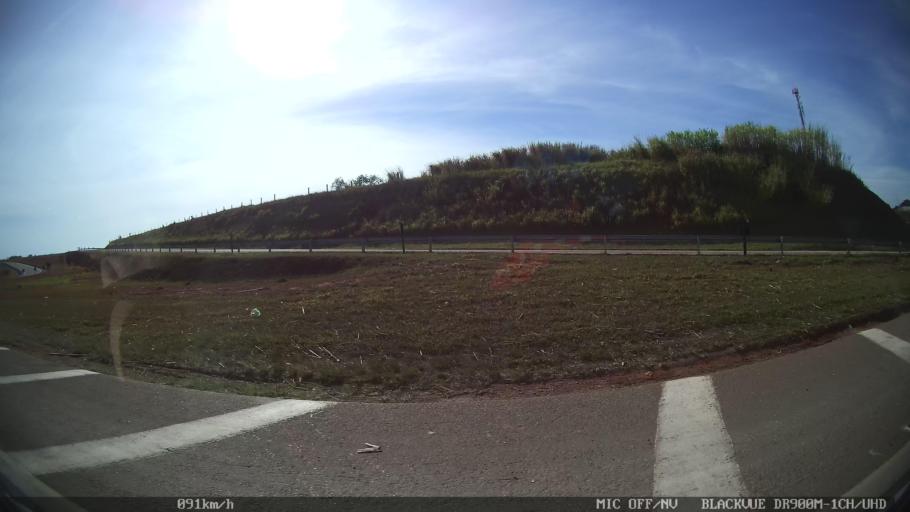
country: BR
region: Sao Paulo
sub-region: Rio Das Pedras
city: Rio das Pedras
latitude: -22.7846
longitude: -47.5859
